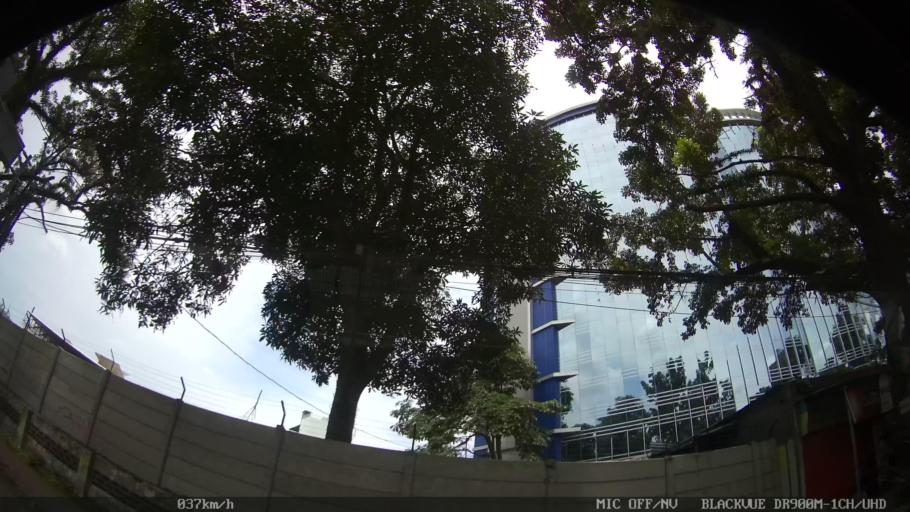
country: ID
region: North Sumatra
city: Medan
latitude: 3.5735
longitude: 98.6623
